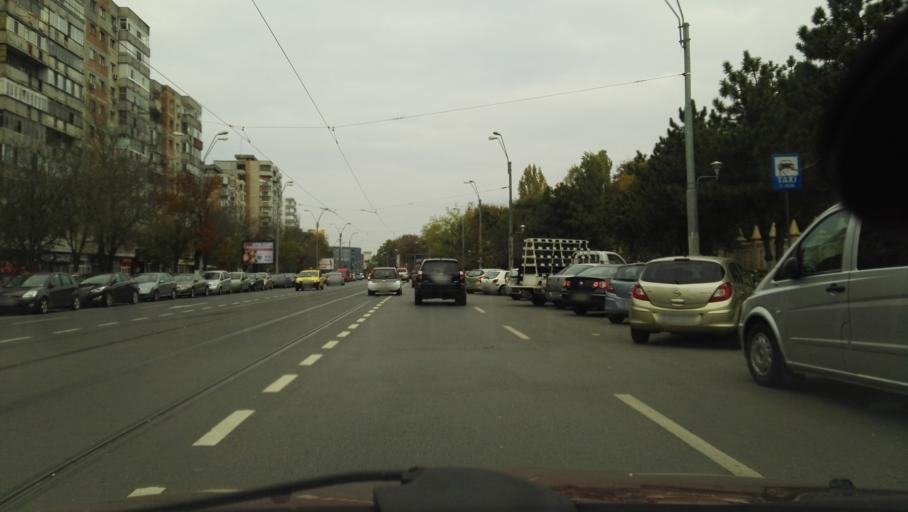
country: RO
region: Bucuresti
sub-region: Municipiul Bucuresti
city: Bucuresti
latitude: 44.3990
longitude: 26.1078
